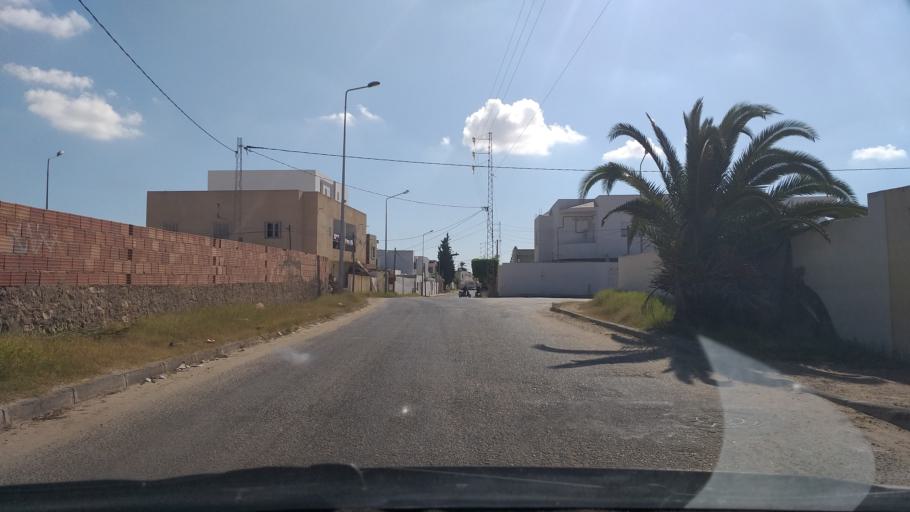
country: TN
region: Safaqis
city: Al Qarmadah
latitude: 34.8018
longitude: 10.7722
